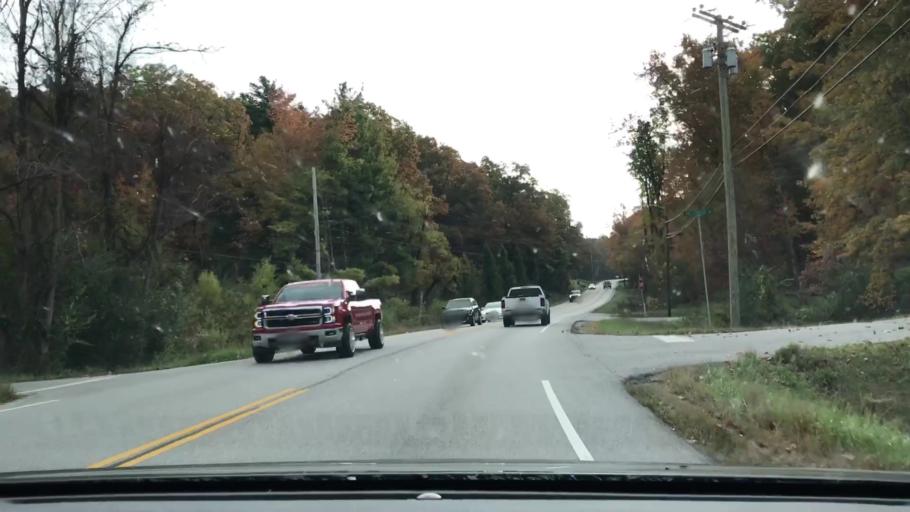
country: US
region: Tennessee
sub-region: Putnam County
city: Monterey
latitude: 36.1403
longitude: -85.2548
